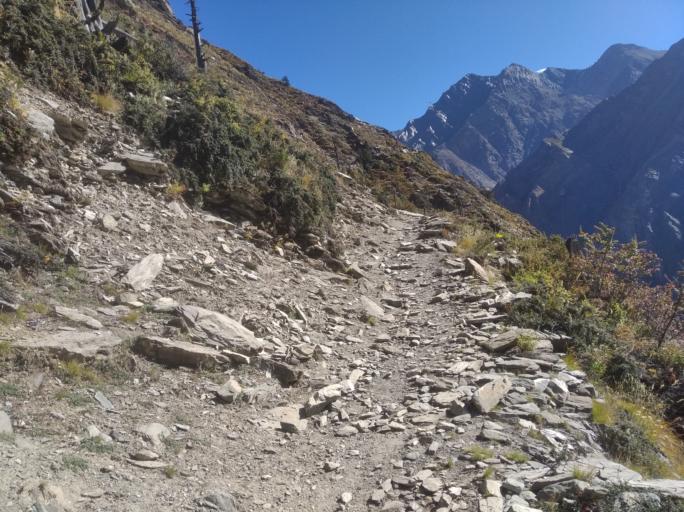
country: NP
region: Western Region
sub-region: Dhawalagiri Zone
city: Jomsom
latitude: 28.9199
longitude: 83.3719
